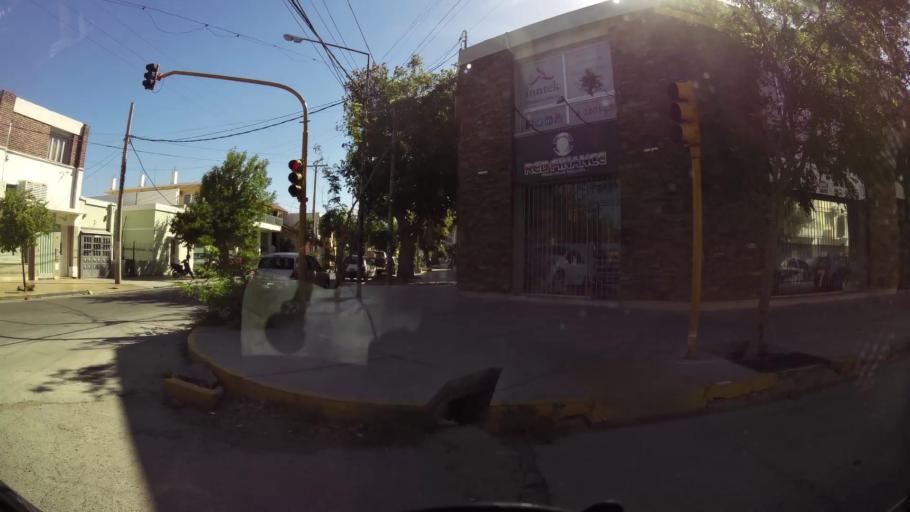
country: AR
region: San Juan
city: San Juan
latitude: -31.5434
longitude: -68.5343
